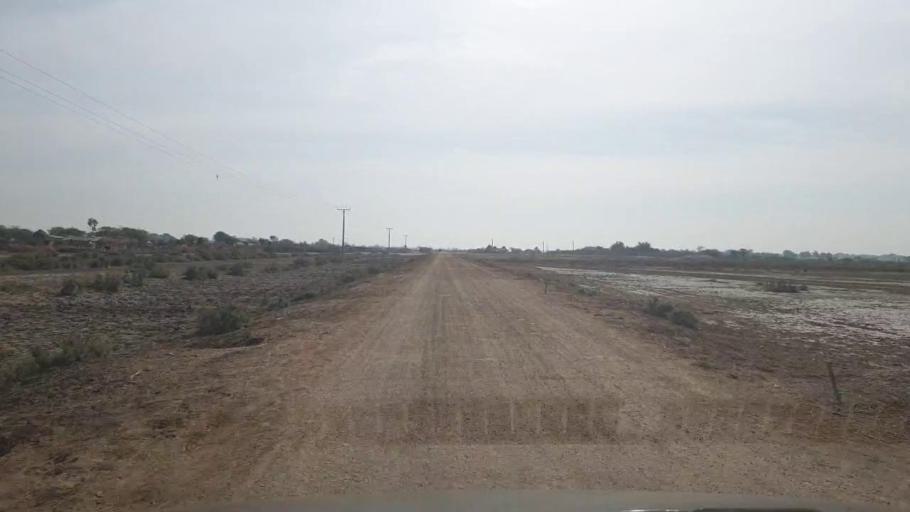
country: PK
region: Sindh
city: Umarkot
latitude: 25.3607
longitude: 69.6508
